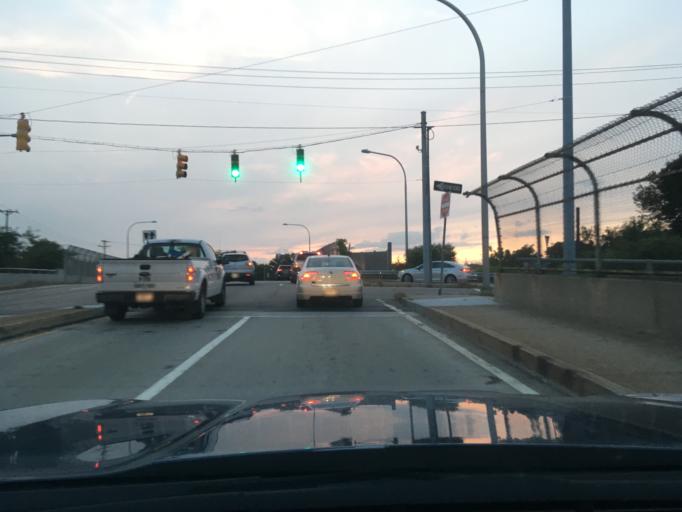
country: US
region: Rhode Island
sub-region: Kent County
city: Warwick
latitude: 41.7114
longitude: -71.4471
